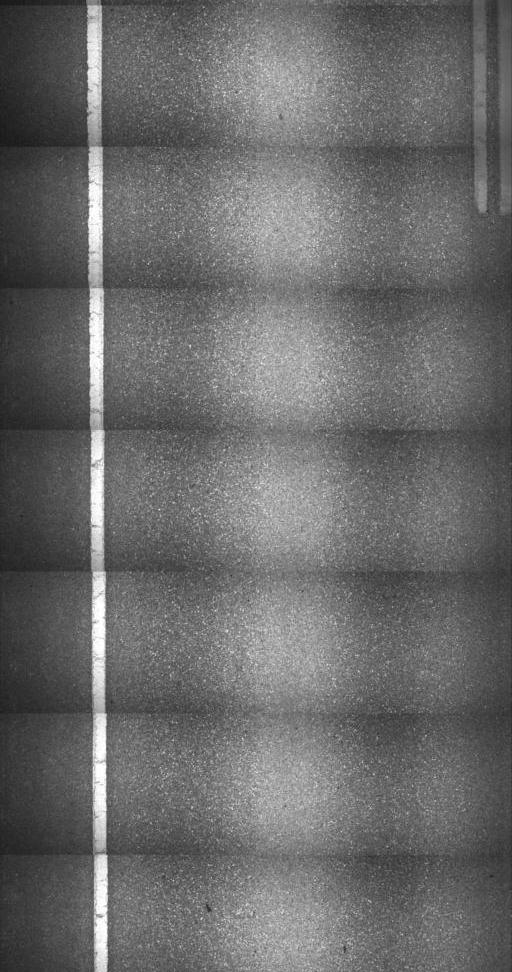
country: US
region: Vermont
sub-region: Addison County
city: Middlebury (village)
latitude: 43.9783
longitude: -73.2049
